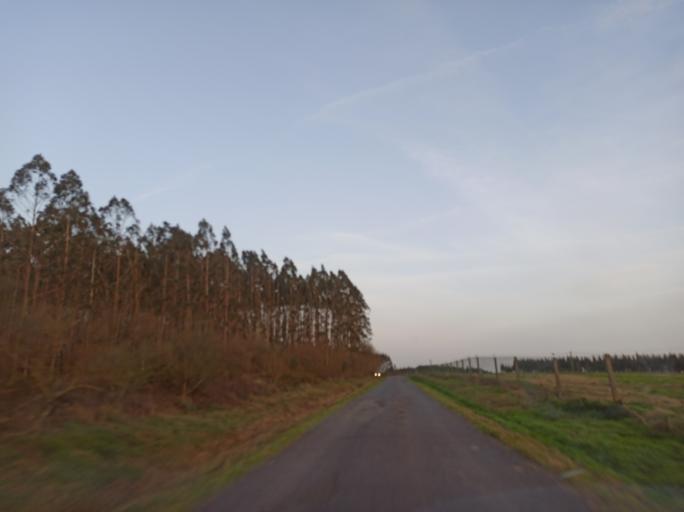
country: ES
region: Galicia
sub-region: Provincia da Coruna
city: Coiros
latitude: 43.1750
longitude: -8.1219
